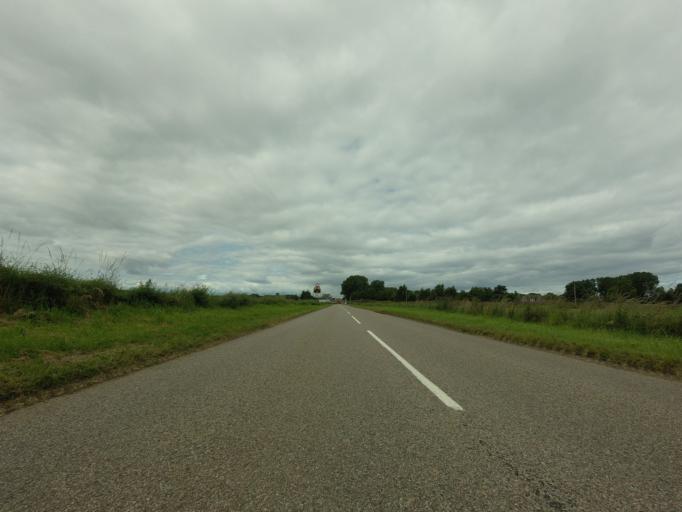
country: GB
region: Scotland
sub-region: Moray
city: Kinloss
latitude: 57.6309
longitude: -3.5559
